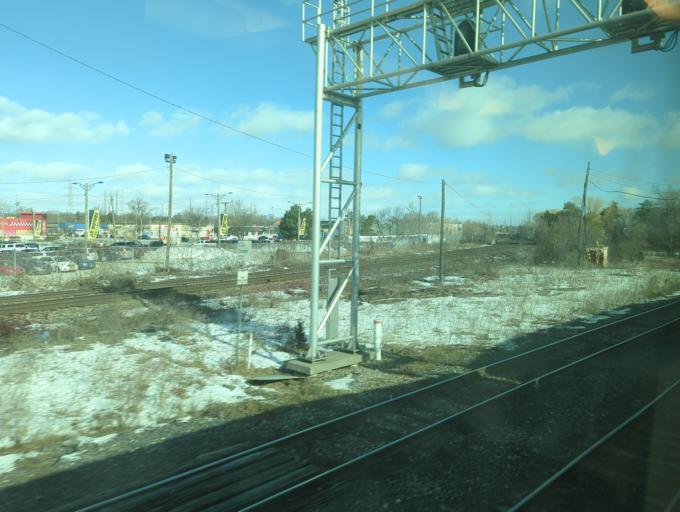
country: CA
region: Ontario
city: Burlington
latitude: 43.3364
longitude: -79.8170
